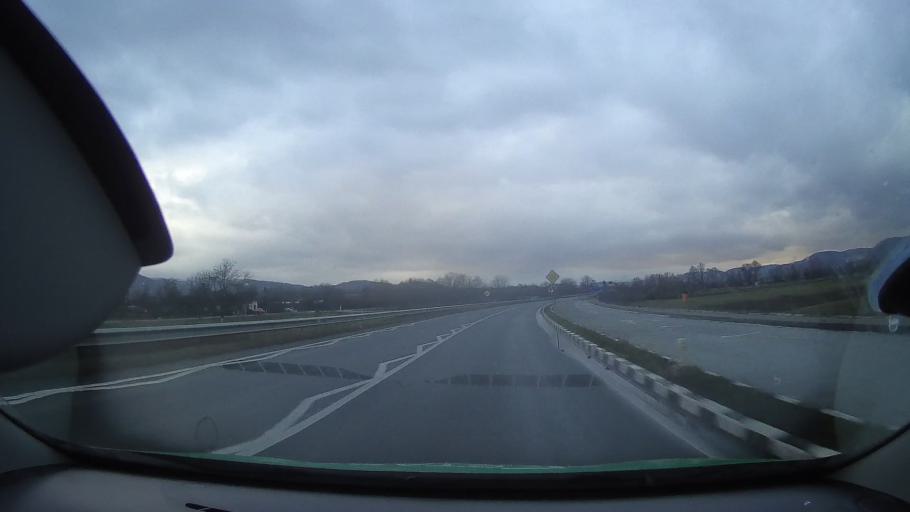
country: RO
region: Hunedoara
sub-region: Comuna Baia de Cris
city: Baia de Cris
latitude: 46.1693
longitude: 22.7302
